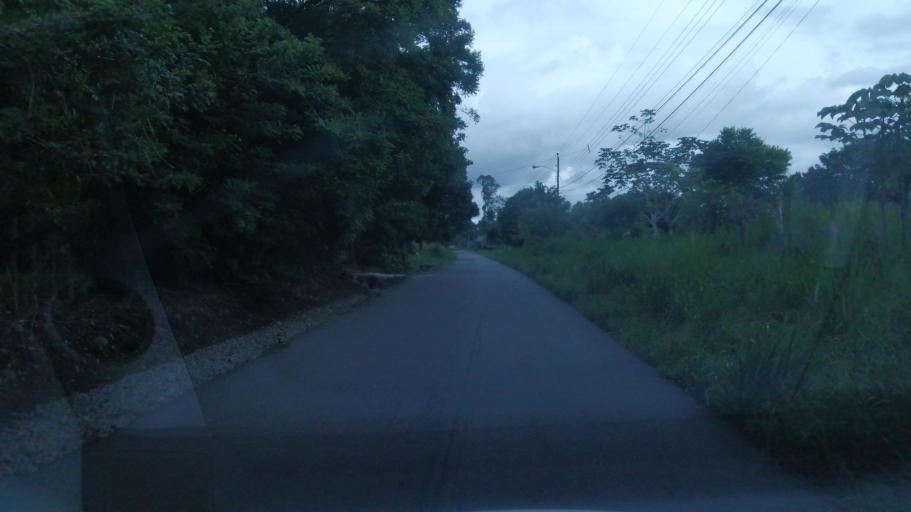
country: PA
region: Chiriqui
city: Tijera
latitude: 8.4503
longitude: -82.5253
